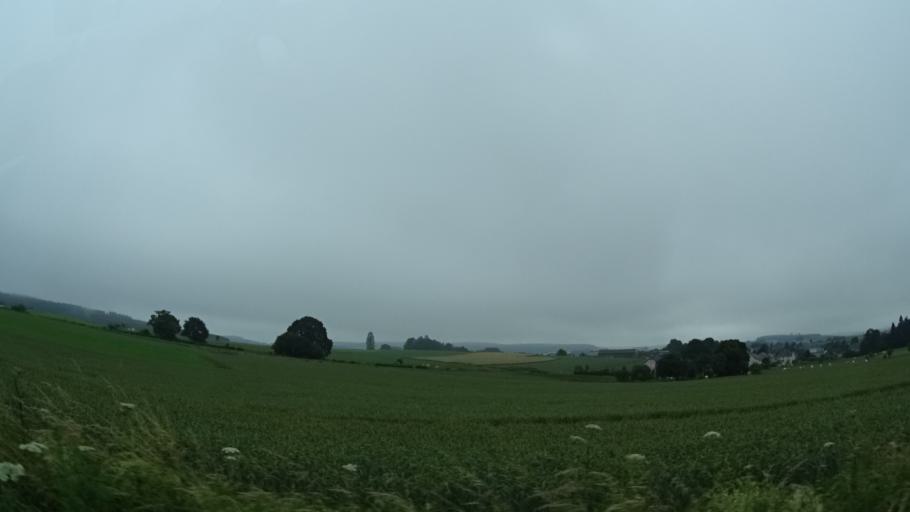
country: BE
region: Wallonia
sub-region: Province du Luxembourg
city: Leglise
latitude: 49.7810
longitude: 5.5612
